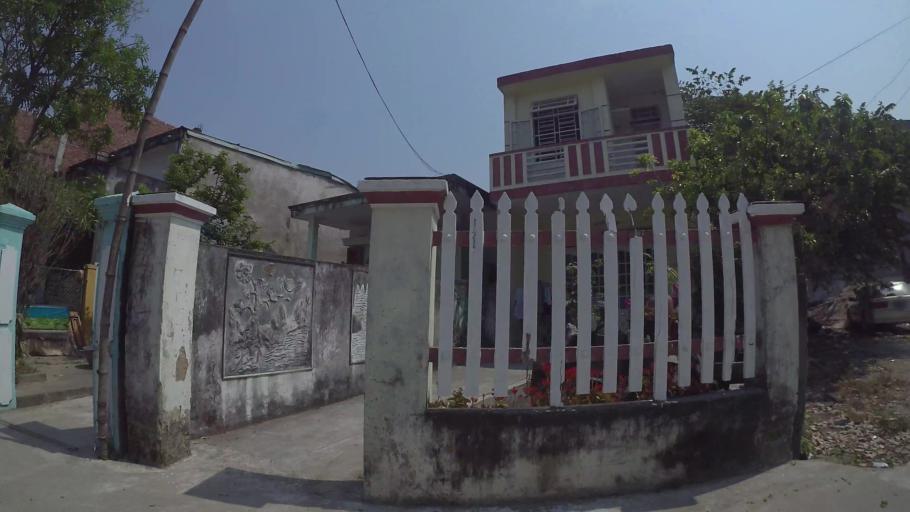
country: VN
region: Da Nang
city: Cam Le
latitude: 15.9956
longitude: 108.1925
